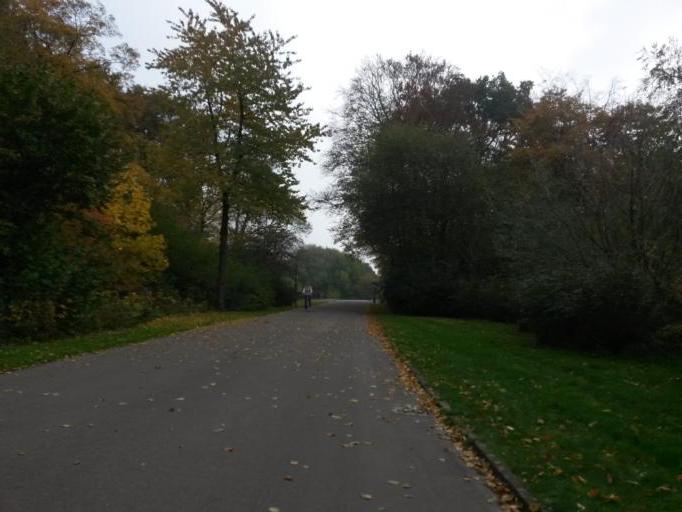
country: DE
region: Bremen
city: Bremen
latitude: 53.0948
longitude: 8.8252
